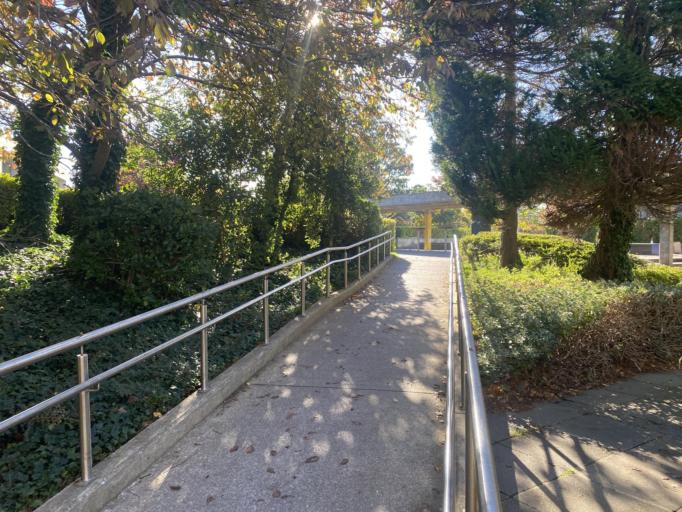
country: IE
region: Leinster
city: Donnybrook
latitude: 53.3064
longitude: -6.2212
